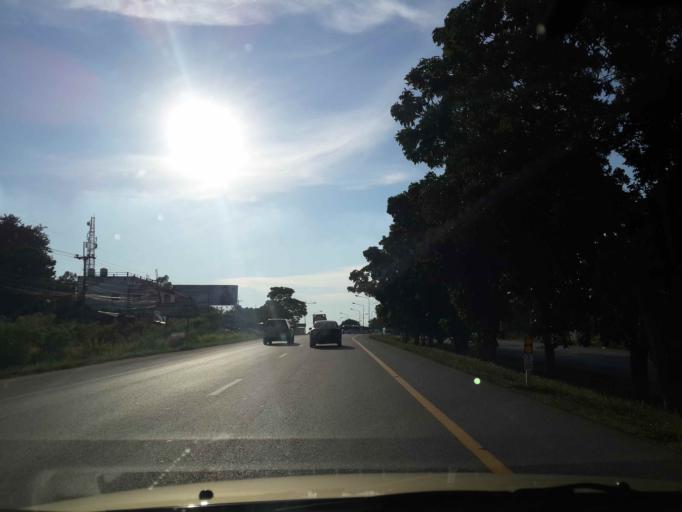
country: TH
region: Chon Buri
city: Bang Lamung
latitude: 12.9835
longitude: 100.9522
